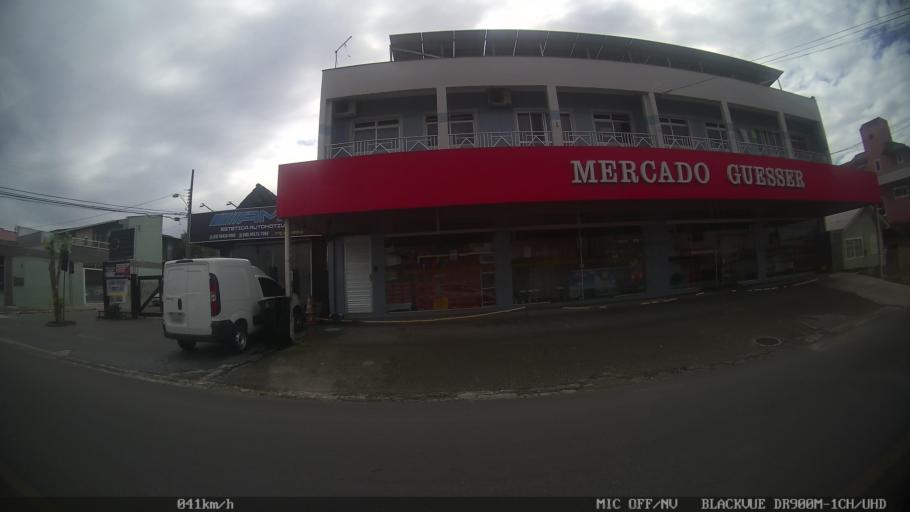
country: BR
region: Santa Catarina
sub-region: Sao Jose
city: Campinas
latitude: -27.5697
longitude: -48.6163
